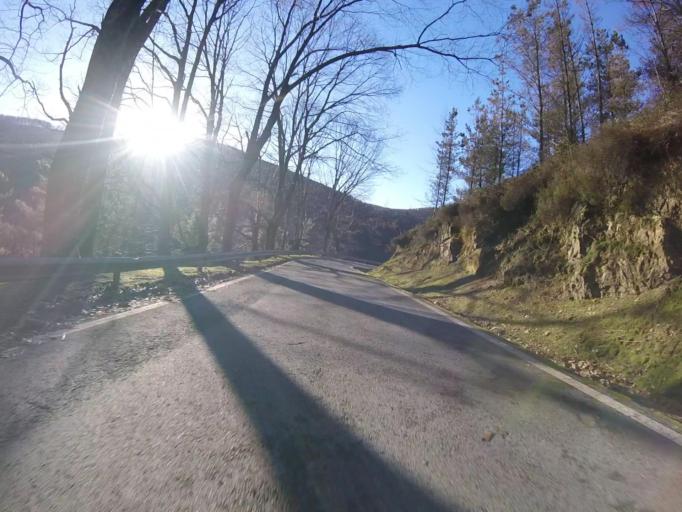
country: ES
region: Navarre
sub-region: Provincia de Navarra
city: Lesaka
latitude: 43.2648
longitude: -1.7677
